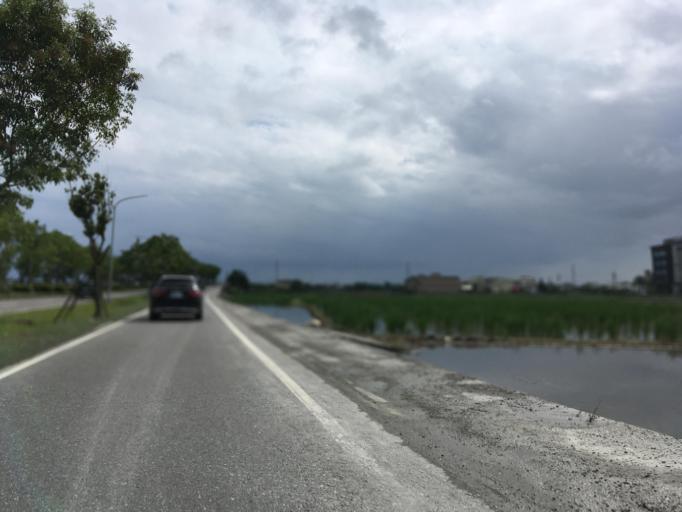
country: TW
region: Taiwan
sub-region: Yilan
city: Yilan
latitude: 24.6777
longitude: 121.7797
